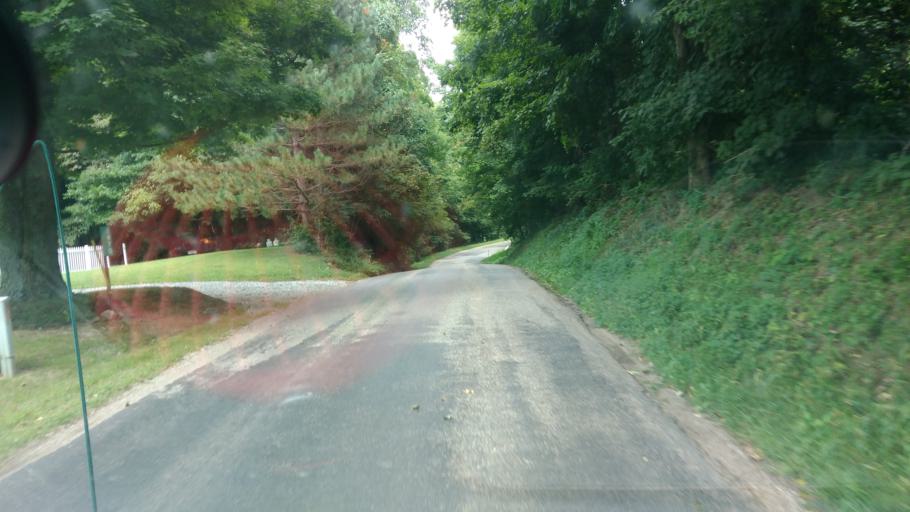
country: US
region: Ohio
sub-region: Ashland County
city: Ashland
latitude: 40.7765
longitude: -82.3641
